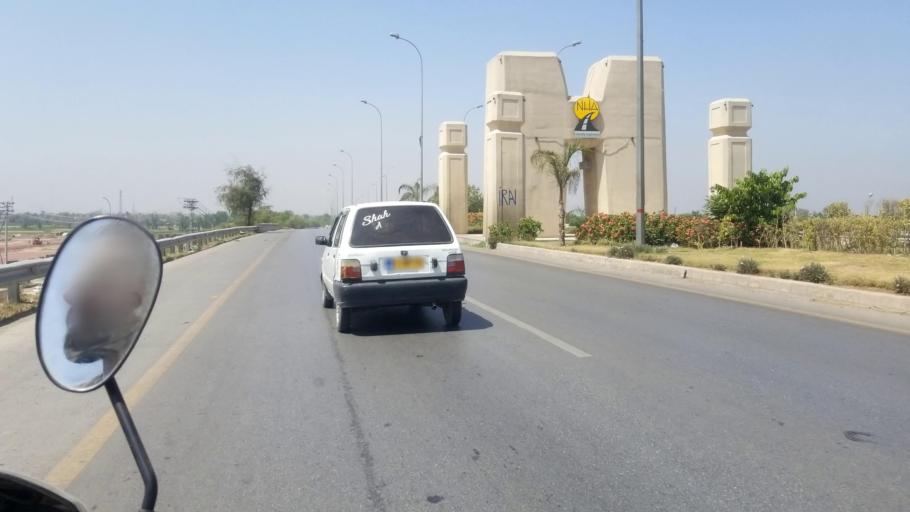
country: PK
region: Khyber Pakhtunkhwa
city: Peshawar
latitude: 34.0263
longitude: 71.6448
